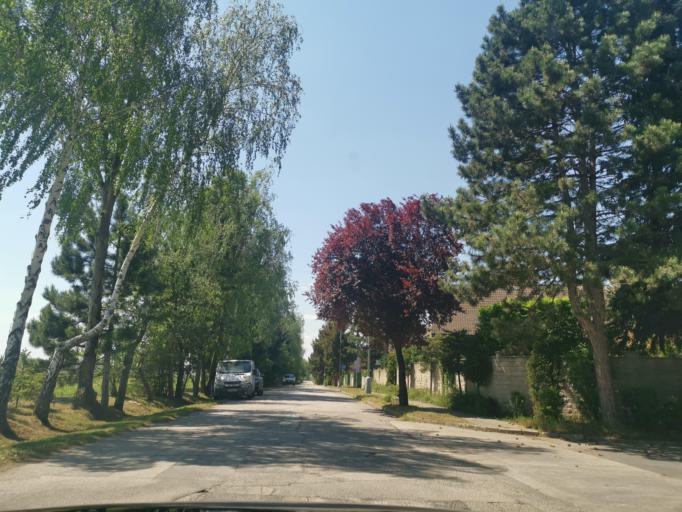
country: SK
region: Trnavsky
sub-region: Okres Senica
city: Senica
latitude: 48.6711
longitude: 17.3685
